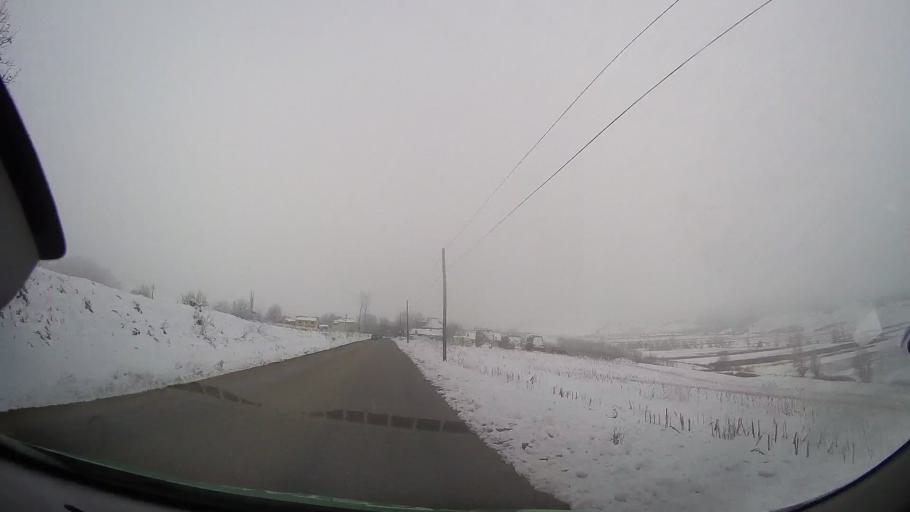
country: RO
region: Bacau
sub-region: Comuna Stanisesti
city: Stanisesti
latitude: 46.4090
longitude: 27.2714
